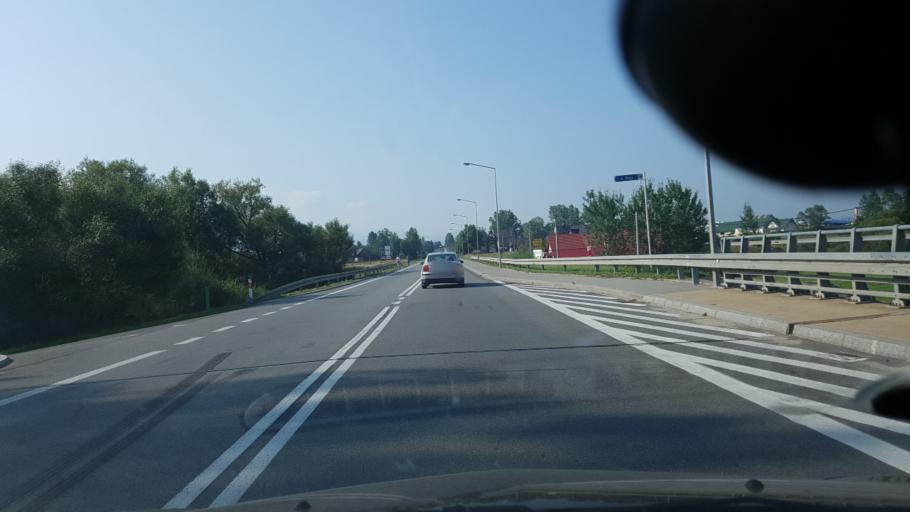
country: PL
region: Lesser Poland Voivodeship
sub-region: Powiat nowotarski
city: Jablonka
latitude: 49.4681
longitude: 19.6921
